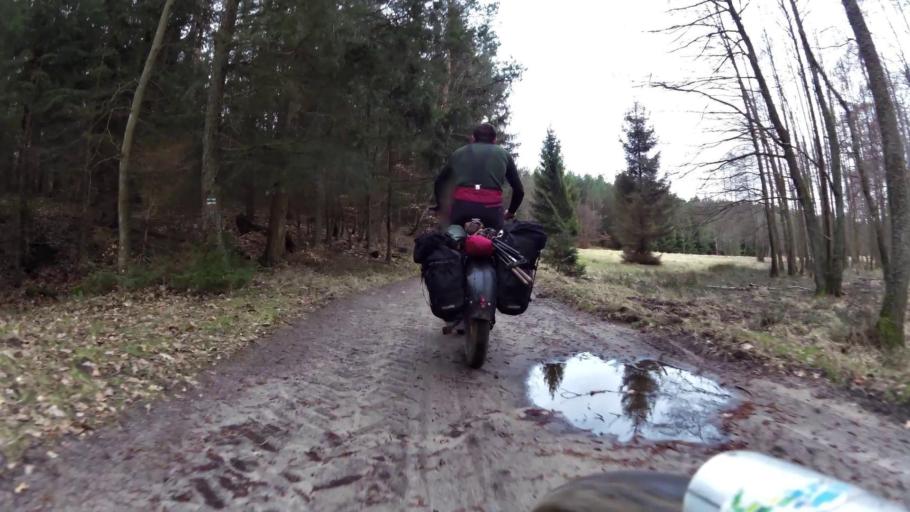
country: PL
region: Pomeranian Voivodeship
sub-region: Powiat bytowski
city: Trzebielino
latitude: 54.1284
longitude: 17.1354
